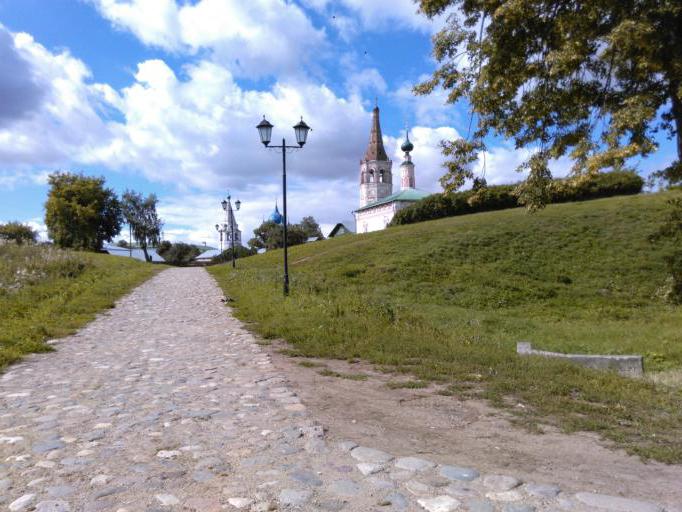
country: RU
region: Vladimir
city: Suzdal'
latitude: 56.4147
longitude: 40.4478
